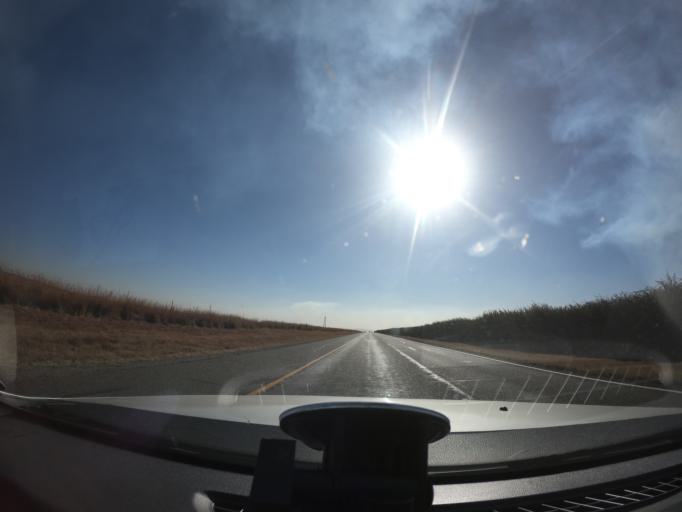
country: ZA
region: Gauteng
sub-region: Sedibeng District Municipality
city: Heidelberg
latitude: -26.4400
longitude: 28.3061
